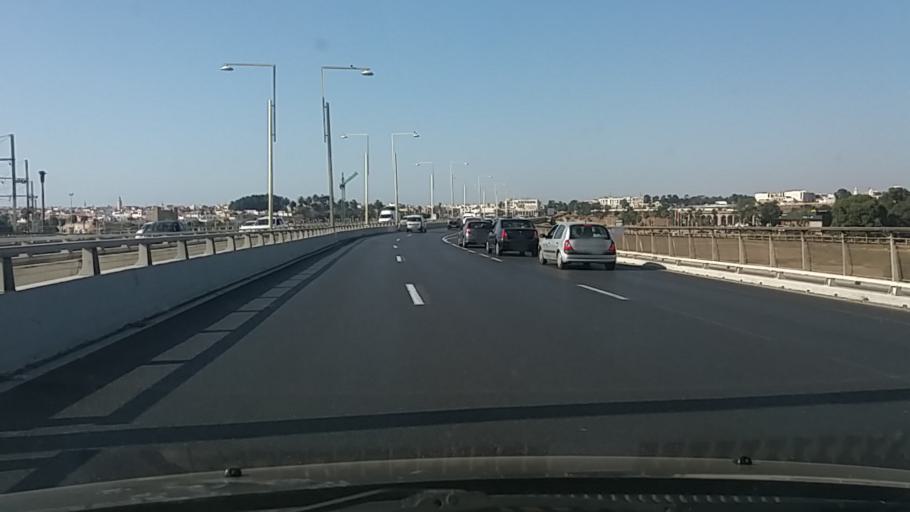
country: MA
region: Rabat-Sale-Zemmour-Zaer
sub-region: Rabat
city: Rabat
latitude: 34.0284
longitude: -6.8193
